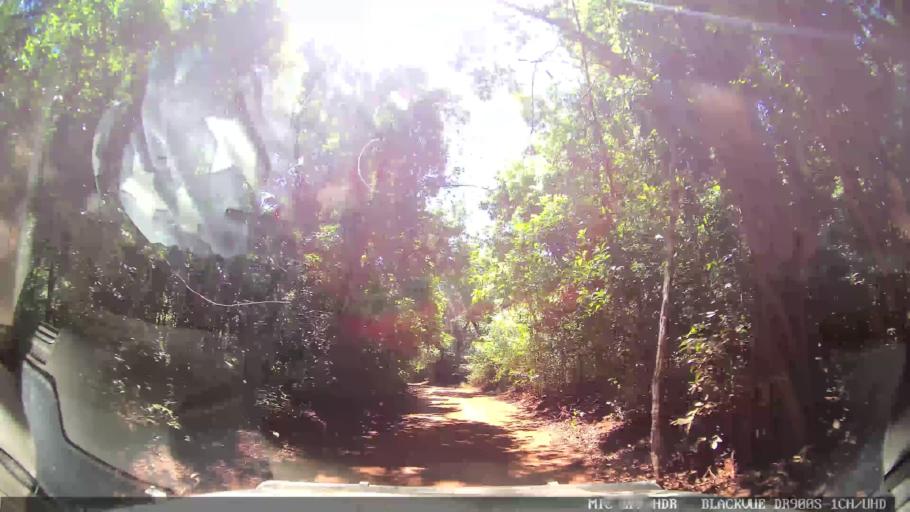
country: AU
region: Queensland
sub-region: Torres
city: Thursday Island
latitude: -10.7784
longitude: 142.4903
